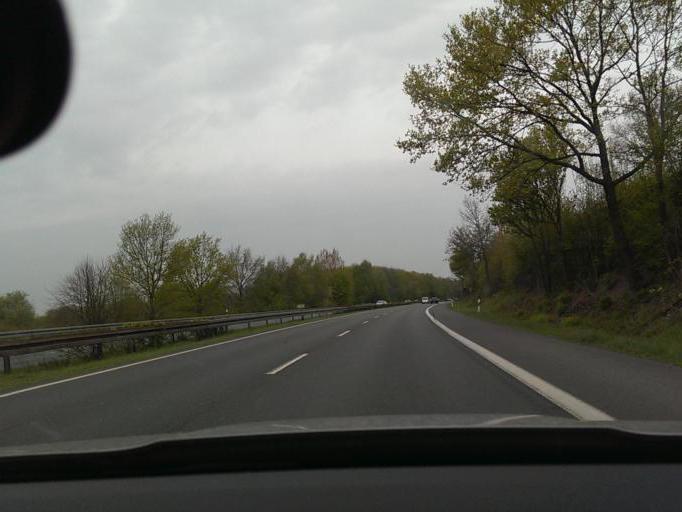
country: DE
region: Lower Saxony
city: Auf der Horst
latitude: 52.3987
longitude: 9.6659
